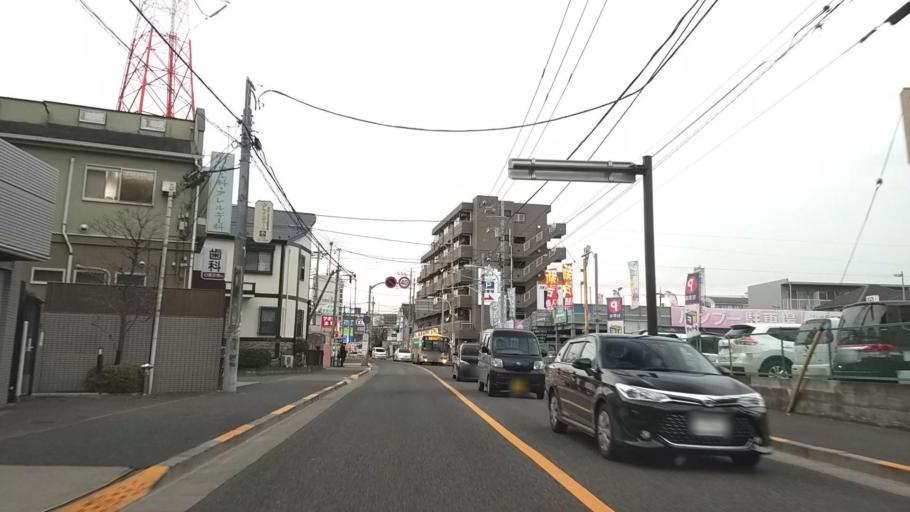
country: JP
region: Tokyo
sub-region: Machida-shi
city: Machida
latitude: 35.5523
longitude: 139.4398
